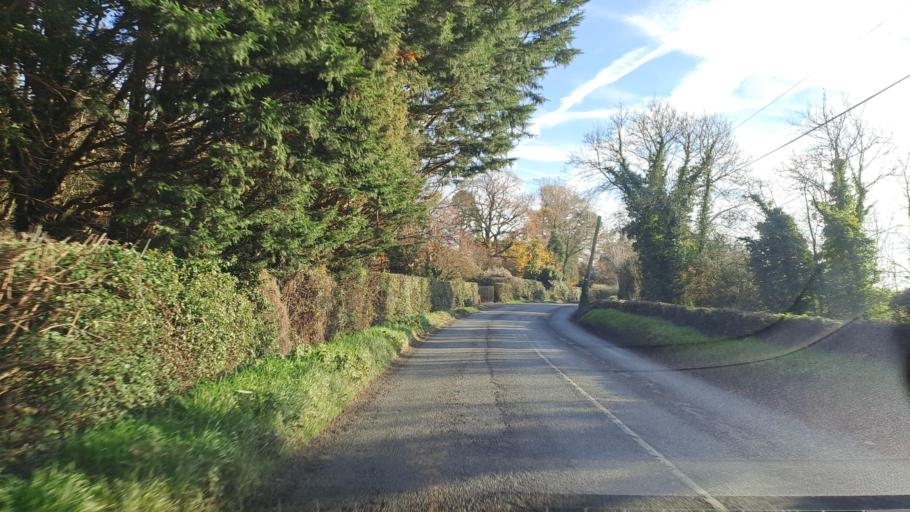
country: IE
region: Ulster
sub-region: County Monaghan
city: Carrickmacross
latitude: 53.8590
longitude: -6.6730
